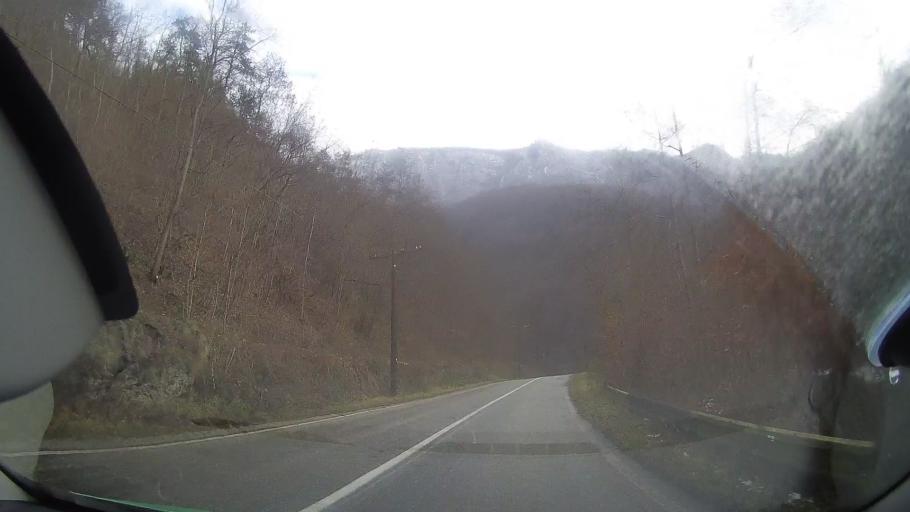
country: RO
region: Alba
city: Salciua de Sus
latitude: 46.4181
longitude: 23.4581
